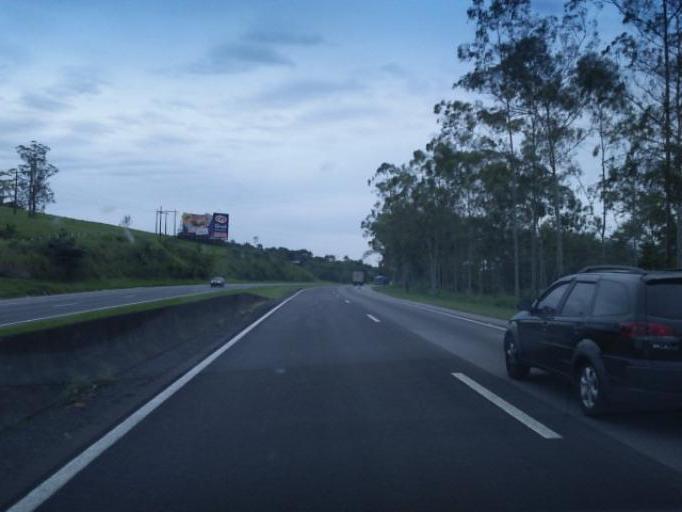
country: BR
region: Sao Paulo
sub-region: Registro
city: Registro
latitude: -24.4178
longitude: -47.7643
